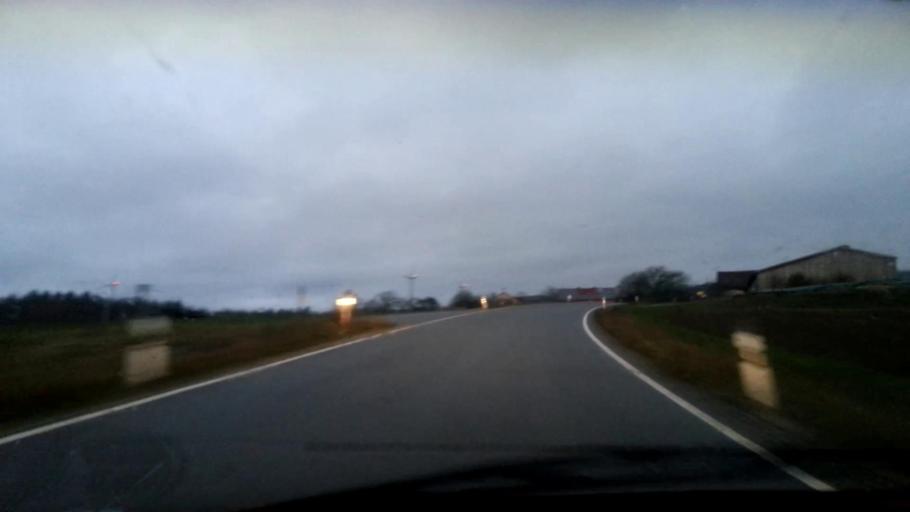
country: DE
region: Bavaria
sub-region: Upper Franconia
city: Poxdorf
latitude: 49.9684
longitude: 11.1289
